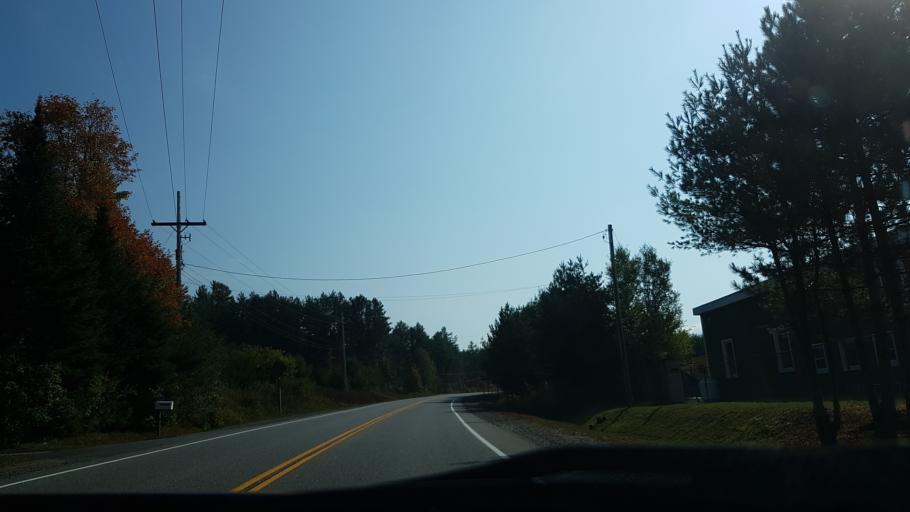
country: CA
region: Ontario
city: Bracebridge
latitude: 44.9850
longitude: -79.2710
